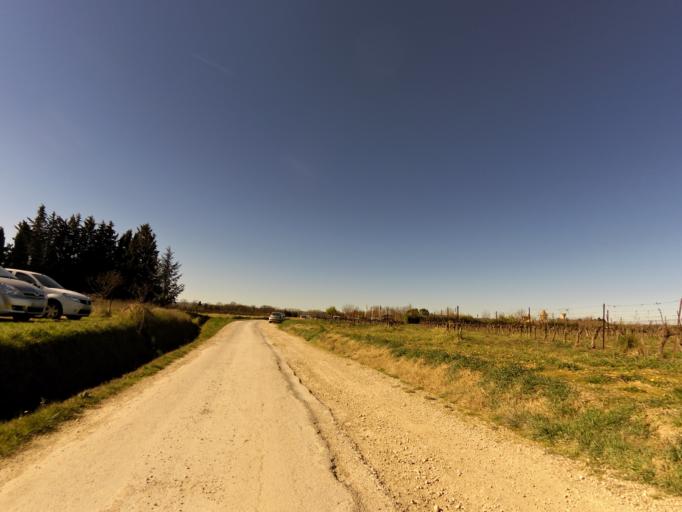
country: FR
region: Languedoc-Roussillon
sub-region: Departement du Gard
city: Saint-Chaptes
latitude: 43.9670
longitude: 4.2734
